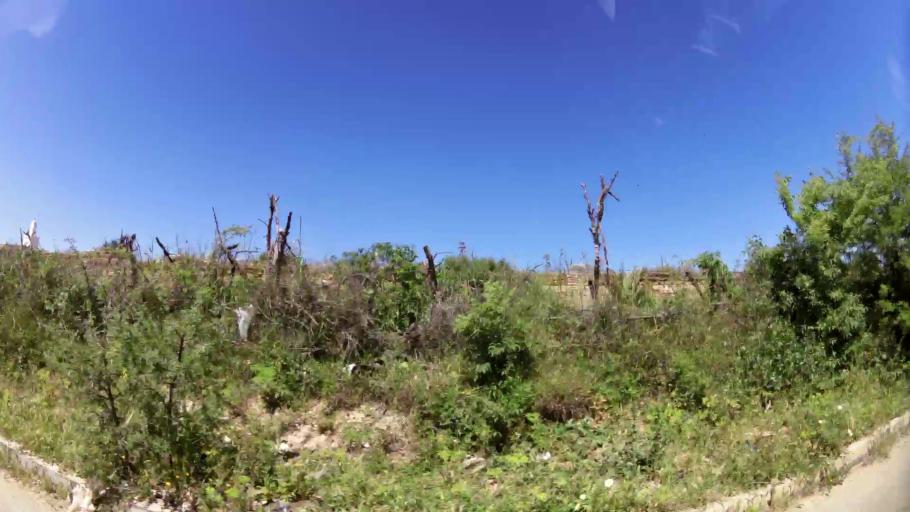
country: MA
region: Meknes-Tafilalet
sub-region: Meknes
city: Meknes
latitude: 33.8645
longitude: -5.5562
